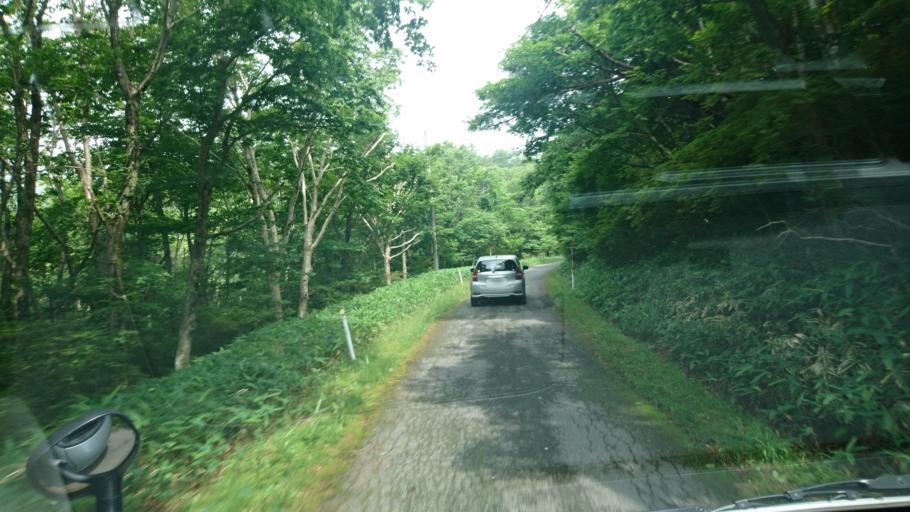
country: JP
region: Iwate
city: Ofunato
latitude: 39.1505
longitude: 141.7543
